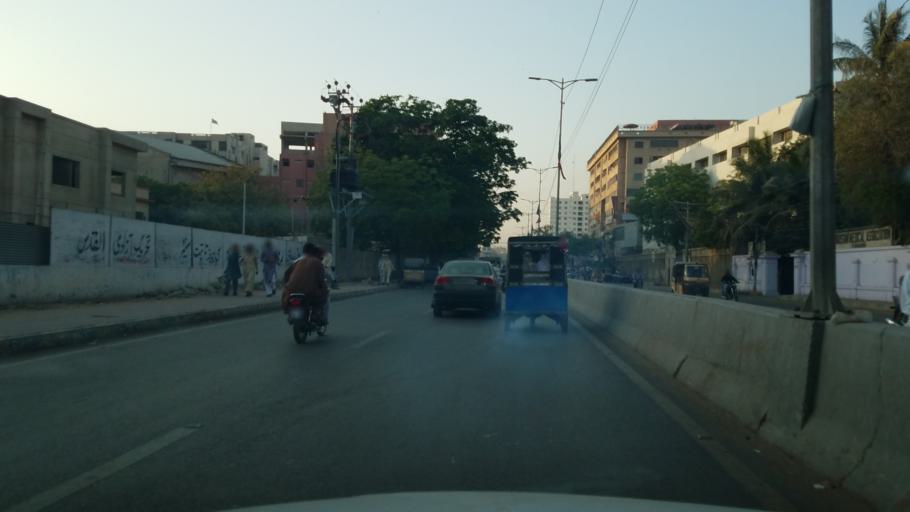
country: PK
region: Sindh
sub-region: Karachi District
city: Karachi
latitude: 24.8658
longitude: 67.0246
